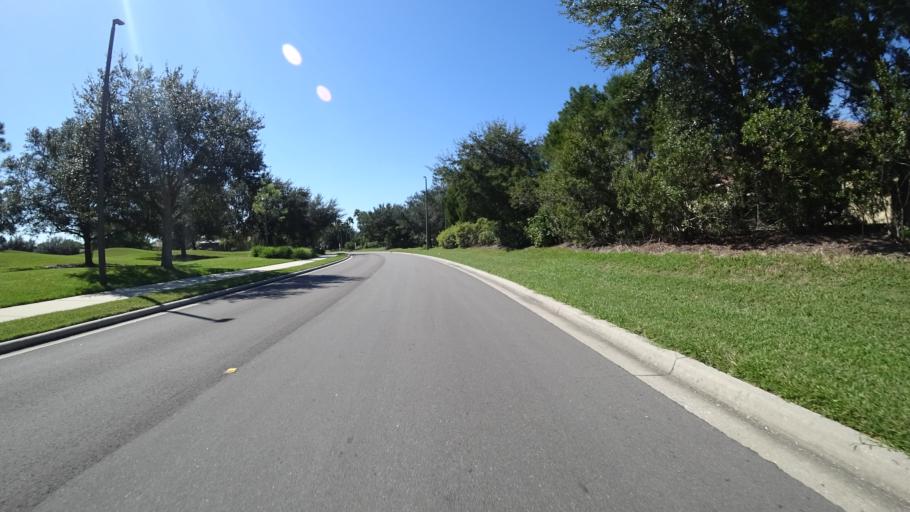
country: US
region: Florida
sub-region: Sarasota County
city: The Meadows
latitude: 27.4142
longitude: -82.4137
